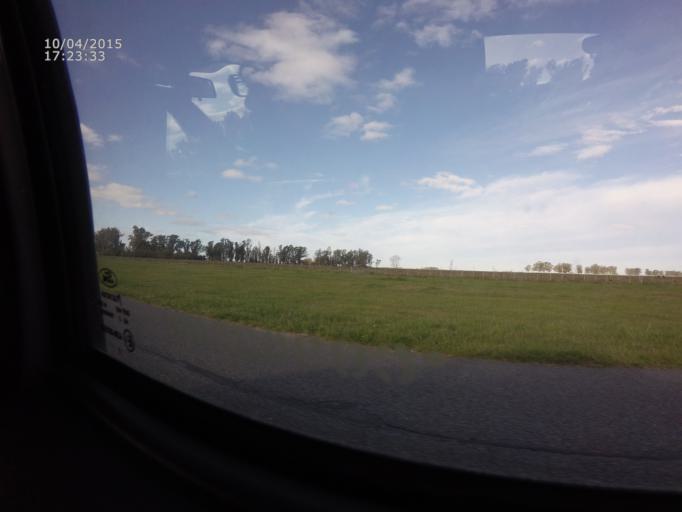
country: AR
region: Buenos Aires
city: Maipu
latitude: -37.0980
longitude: -57.8281
